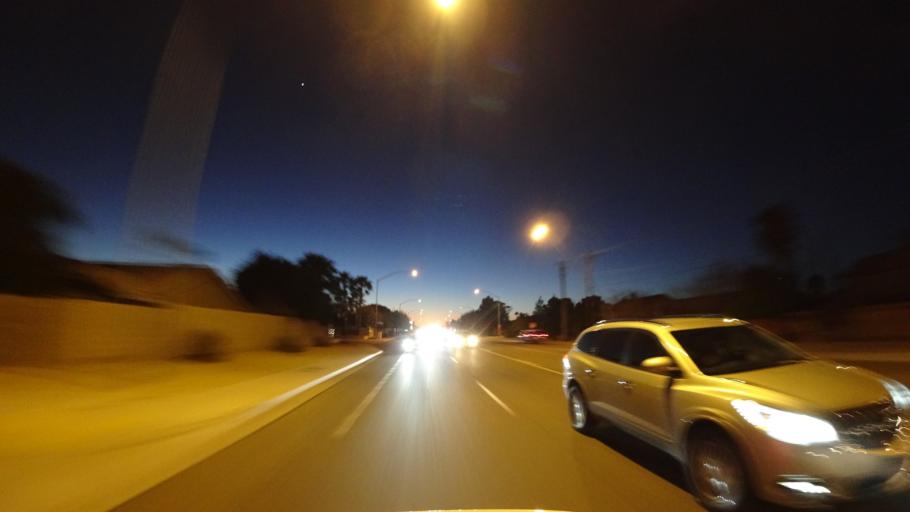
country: US
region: Arizona
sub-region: Maricopa County
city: Mesa
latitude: 33.4517
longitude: -111.7833
